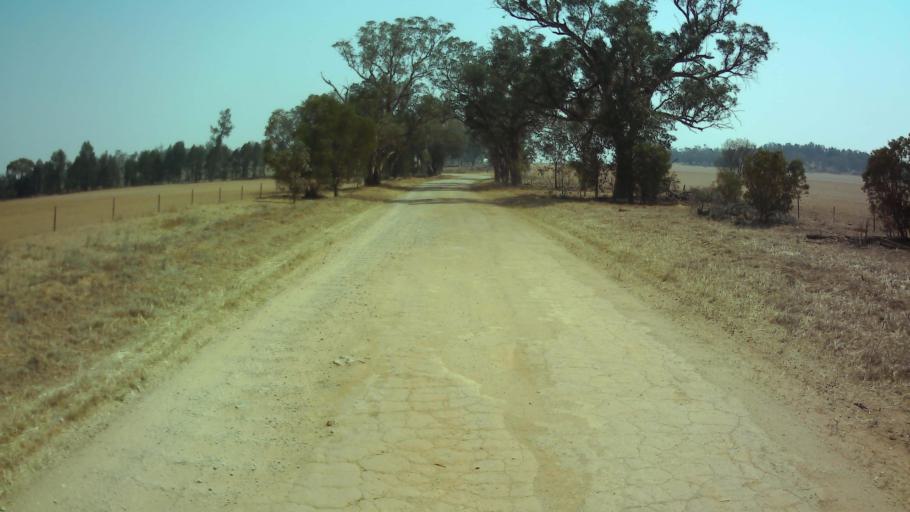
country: AU
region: New South Wales
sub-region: Weddin
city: Grenfell
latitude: -33.6482
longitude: 148.2701
